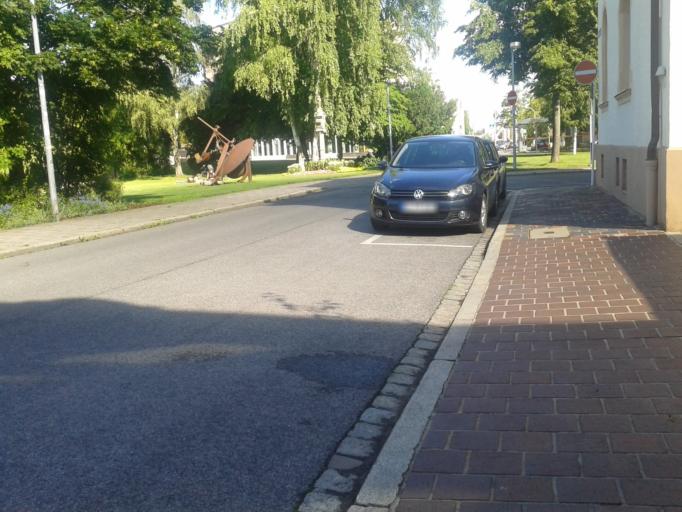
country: DE
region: Bavaria
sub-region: Upper Franconia
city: Bamberg
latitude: 49.8959
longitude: 10.8804
